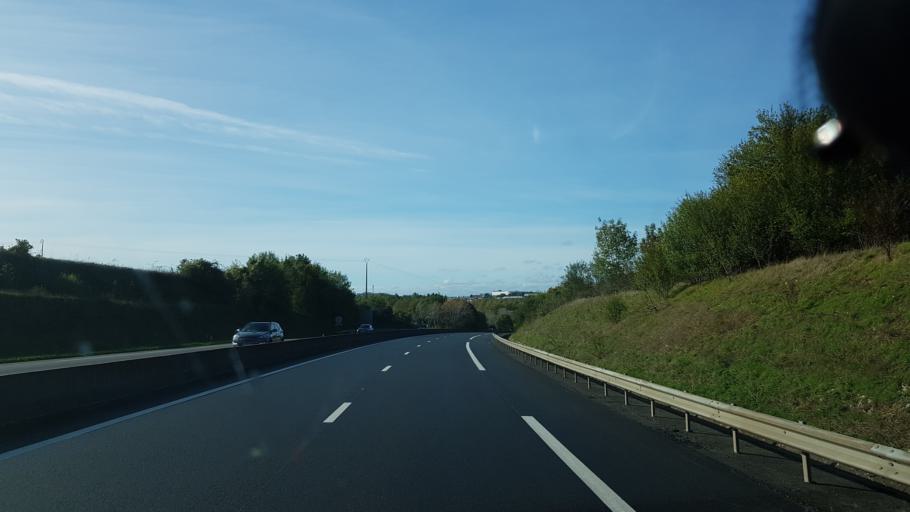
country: FR
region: Poitou-Charentes
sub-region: Departement de la Charente
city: Champniers
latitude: 45.6866
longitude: 0.2003
